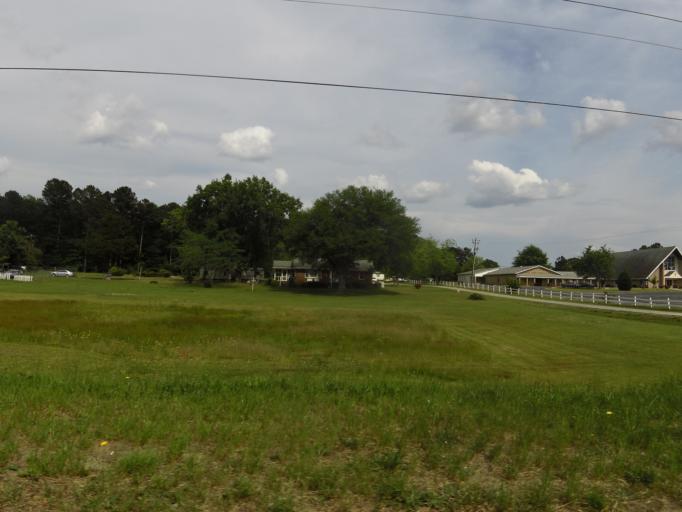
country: US
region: Georgia
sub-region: McDuffie County
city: Thomson
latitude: 33.4931
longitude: -82.5042
